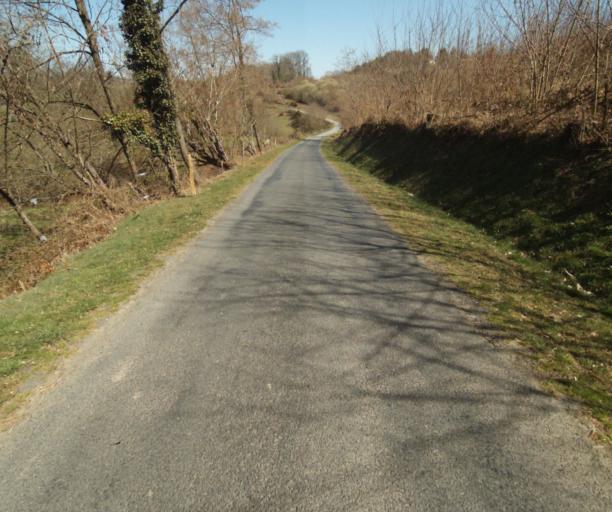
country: FR
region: Limousin
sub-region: Departement de la Correze
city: Saint-Mexant
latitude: 45.2957
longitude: 1.6427
